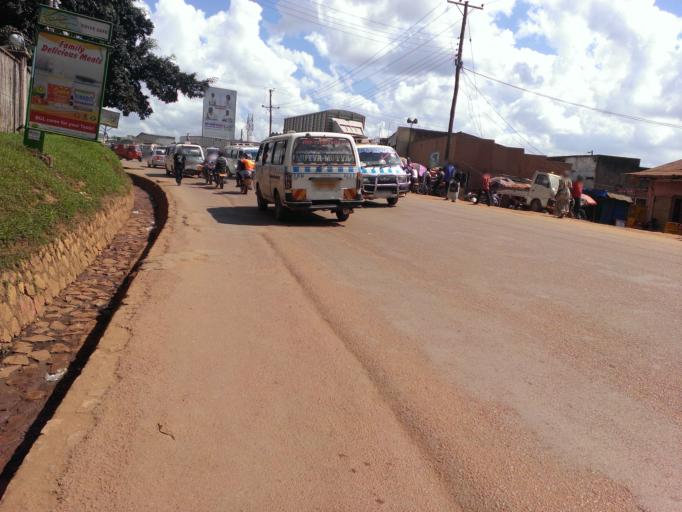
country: UG
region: Central Region
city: Kampala Central Division
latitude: 0.3316
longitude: 32.5567
